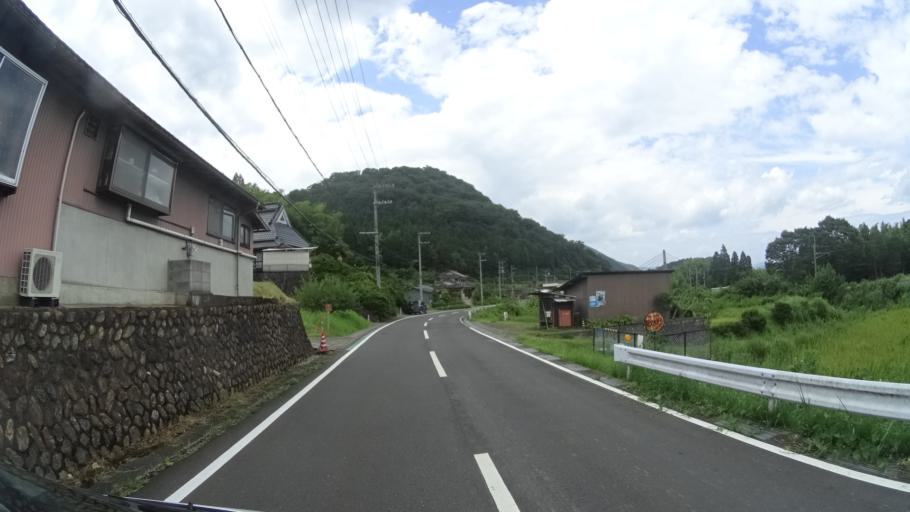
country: JP
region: Kyoto
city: Ayabe
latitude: 35.2885
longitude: 135.2729
